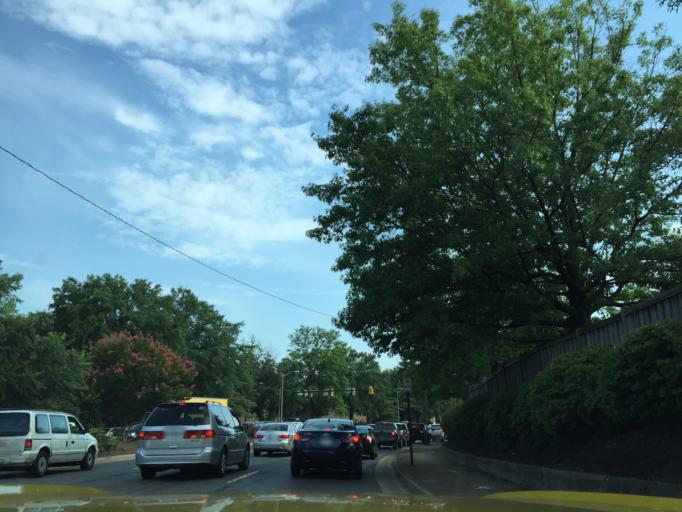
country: US
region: Virginia
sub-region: City of Alexandria
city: Alexandria
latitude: 38.8017
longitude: -77.0514
